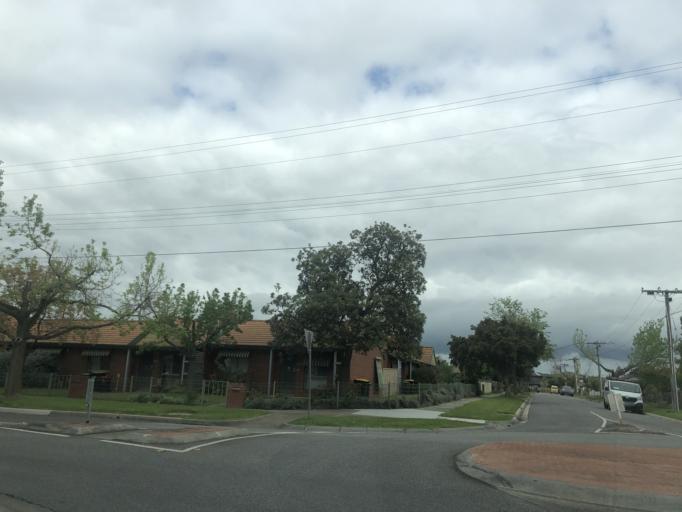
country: AU
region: Victoria
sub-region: Greater Dandenong
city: Dandenong North
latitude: -37.9669
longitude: 145.2102
